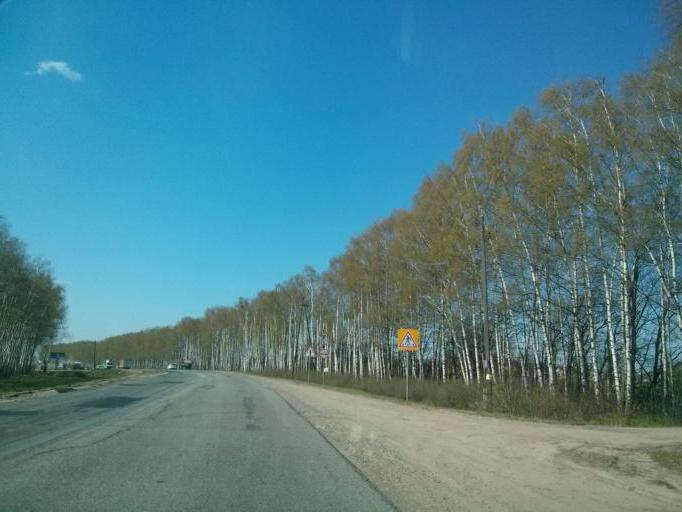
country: RU
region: Nizjnij Novgorod
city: Nizhniy Novgorod
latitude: 56.2144
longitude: 43.9639
